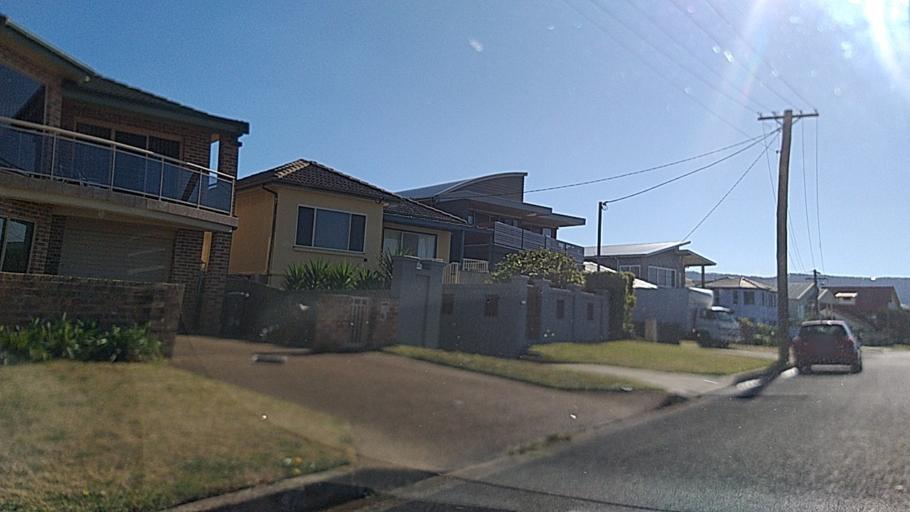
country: AU
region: New South Wales
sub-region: Wollongong
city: Bulli
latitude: -34.3523
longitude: 150.9191
